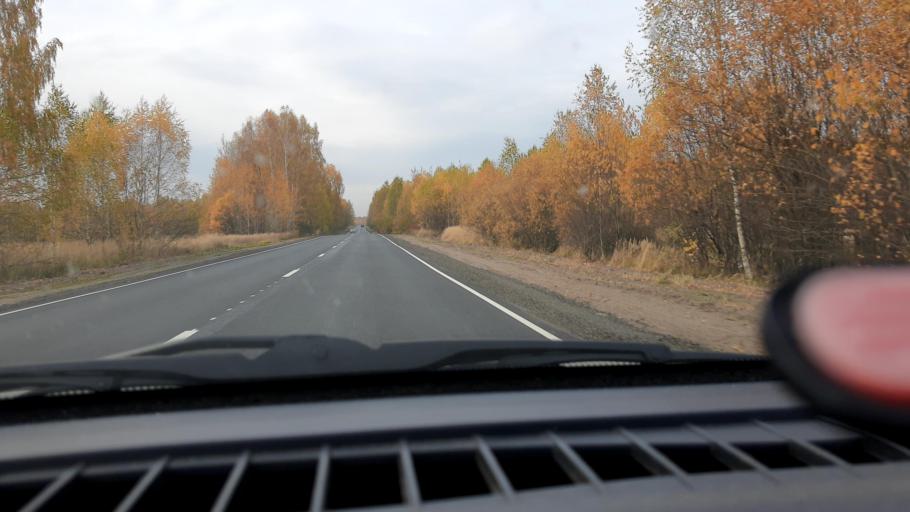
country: RU
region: Nizjnij Novgorod
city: Novaya Balakhna
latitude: 56.5651
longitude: 43.7210
